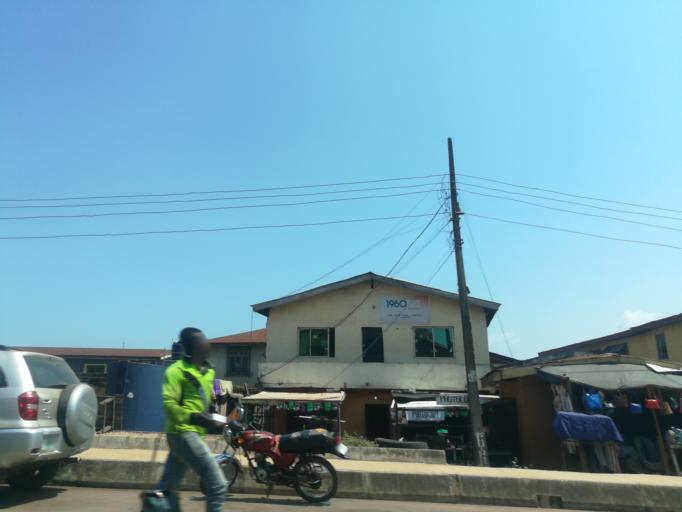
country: NG
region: Ogun
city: Abeokuta
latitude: 7.1670
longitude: 3.3578
